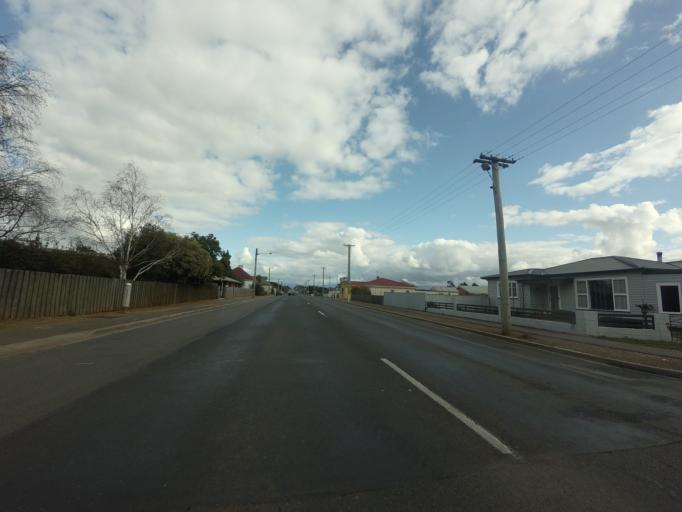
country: AU
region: Tasmania
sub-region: Northern Midlands
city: Longford
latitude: -41.6022
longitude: 147.1197
